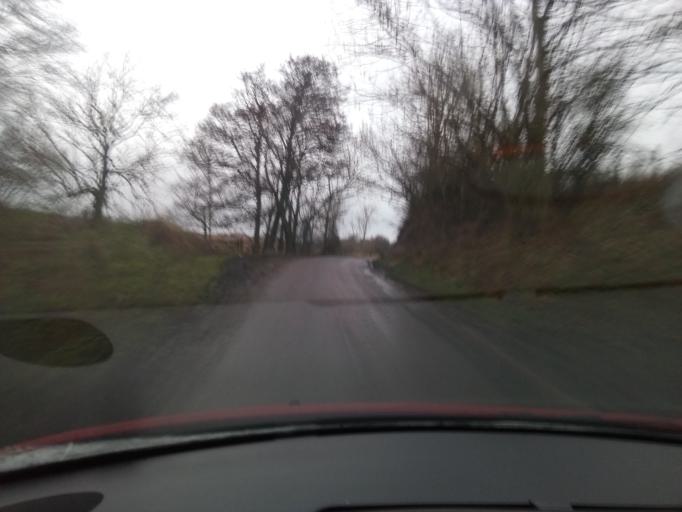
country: GB
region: Scotland
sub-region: The Scottish Borders
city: Kelso
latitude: 55.5459
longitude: -2.4347
